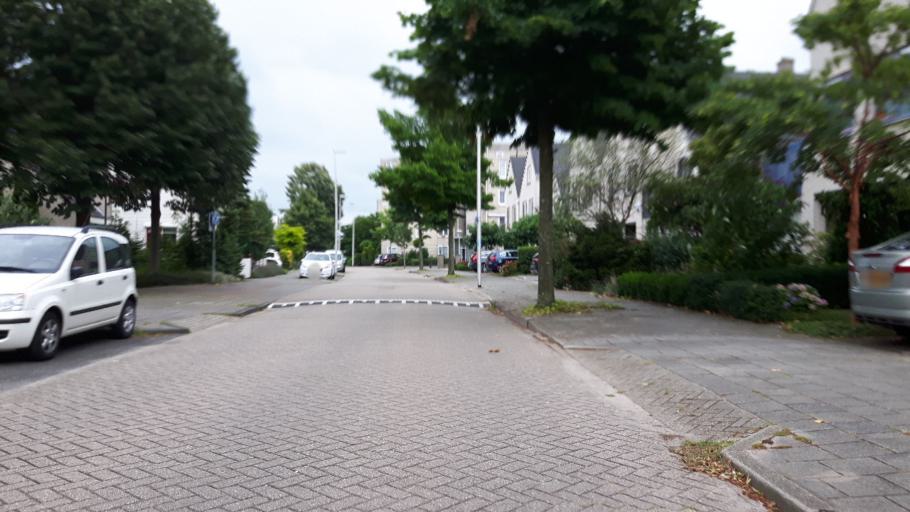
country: NL
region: South Holland
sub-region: Gemeente Alphen aan den Rijn
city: Alphen aan den Rijn
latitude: 52.1219
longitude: 4.6666
